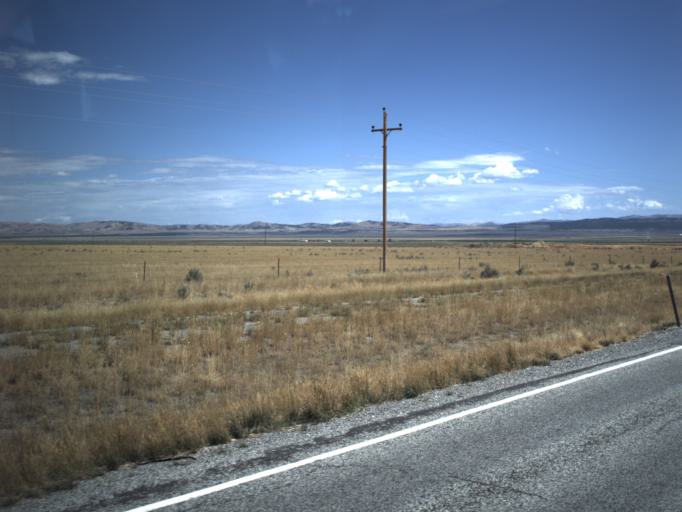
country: US
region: Idaho
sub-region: Oneida County
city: Malad City
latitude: 41.9659
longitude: -112.9846
